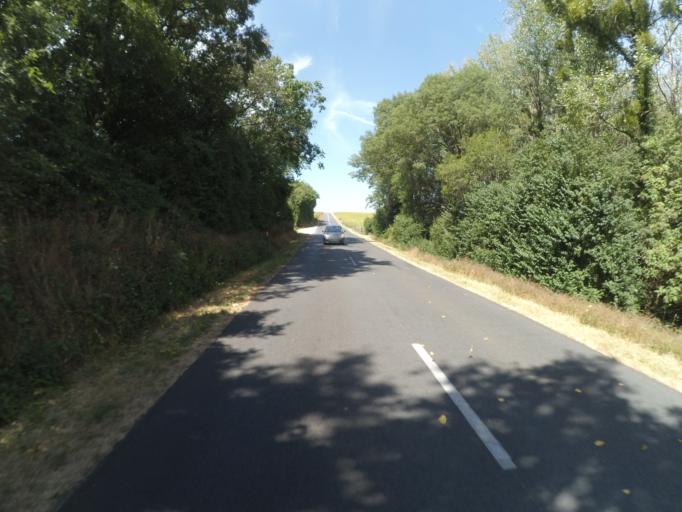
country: FR
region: Poitou-Charentes
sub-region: Departement de la Vienne
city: Saint-Maurice-la-Clouere
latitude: 46.3352
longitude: 0.4649
